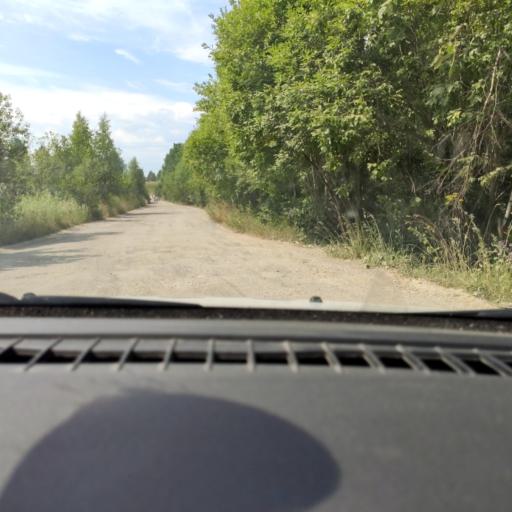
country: RU
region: Perm
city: Polazna
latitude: 58.1814
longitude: 56.4196
